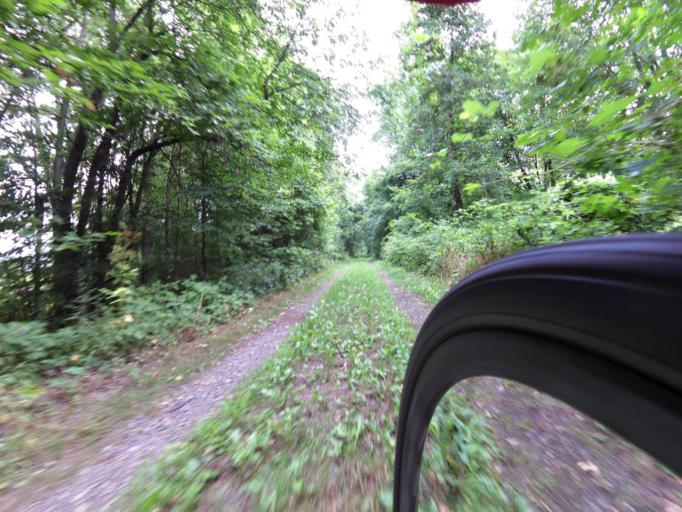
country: CA
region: Ontario
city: Perth
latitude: 44.6439
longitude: -76.2311
